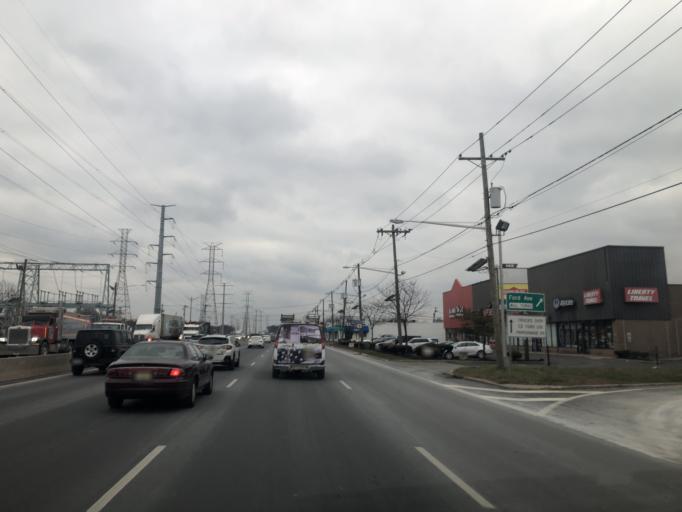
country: US
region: New Jersey
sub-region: Middlesex County
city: Fords
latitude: 40.5497
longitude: -74.3228
